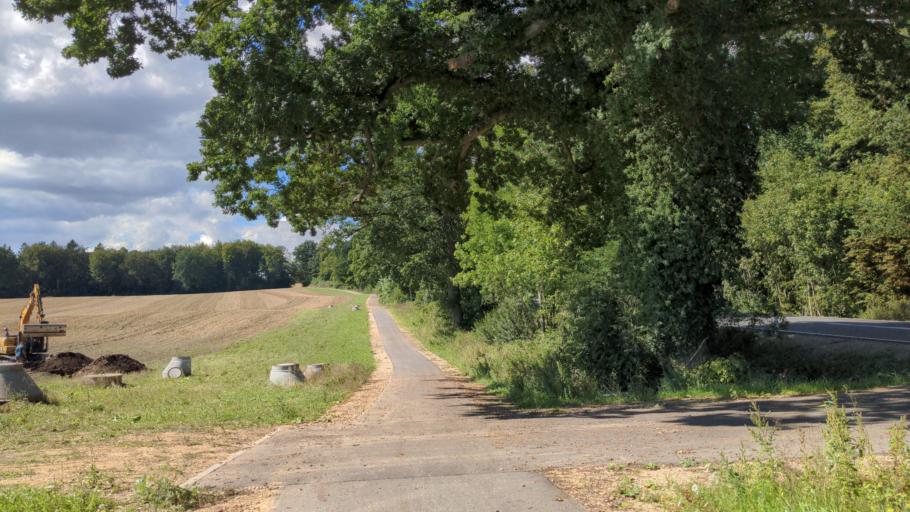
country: DE
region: Schleswig-Holstein
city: Beschendorf
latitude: 54.2057
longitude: 10.8479
